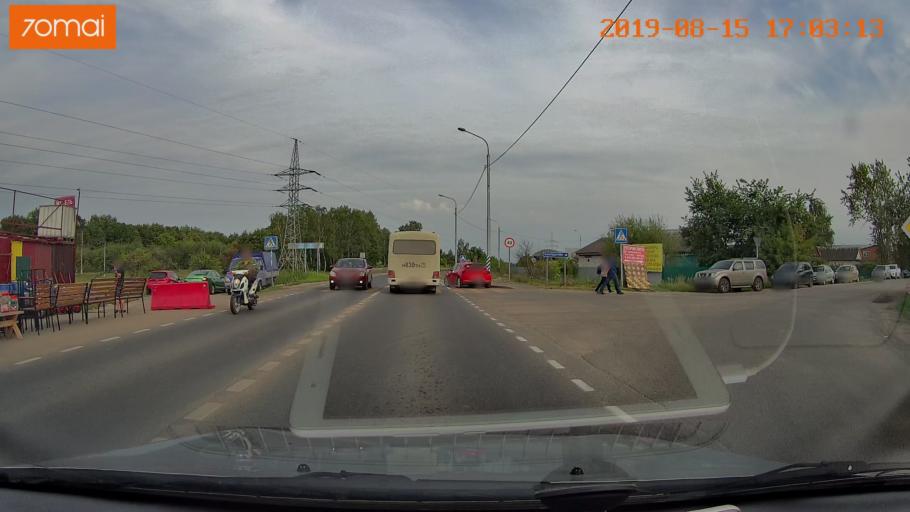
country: RU
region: Moskovskaya
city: Malyshevo
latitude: 55.4823
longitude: 38.4000
